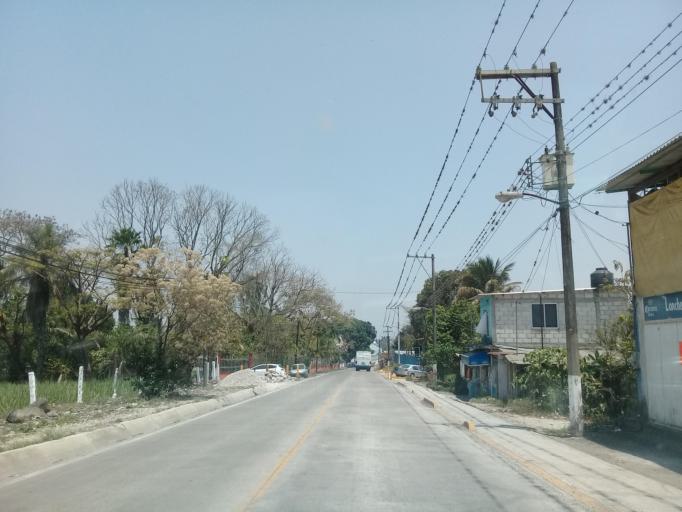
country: MX
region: Veracruz
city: Paraje Nuevo
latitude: 18.8729
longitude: -96.8696
